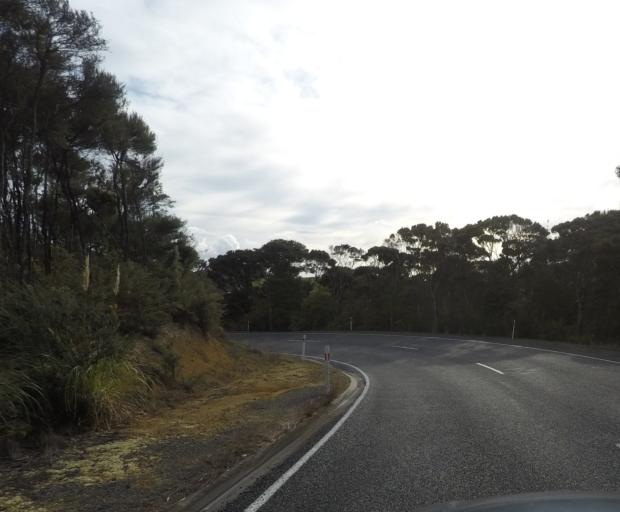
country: NZ
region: Northland
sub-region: Whangarei
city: Ruakaka
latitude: -36.0597
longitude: 174.5636
